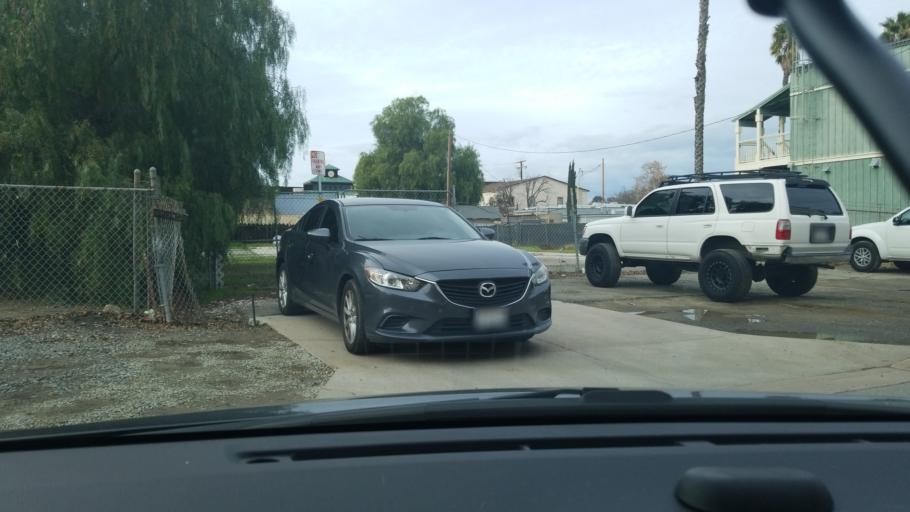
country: US
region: California
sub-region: Riverside County
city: Temecula
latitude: 33.4922
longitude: -117.1485
